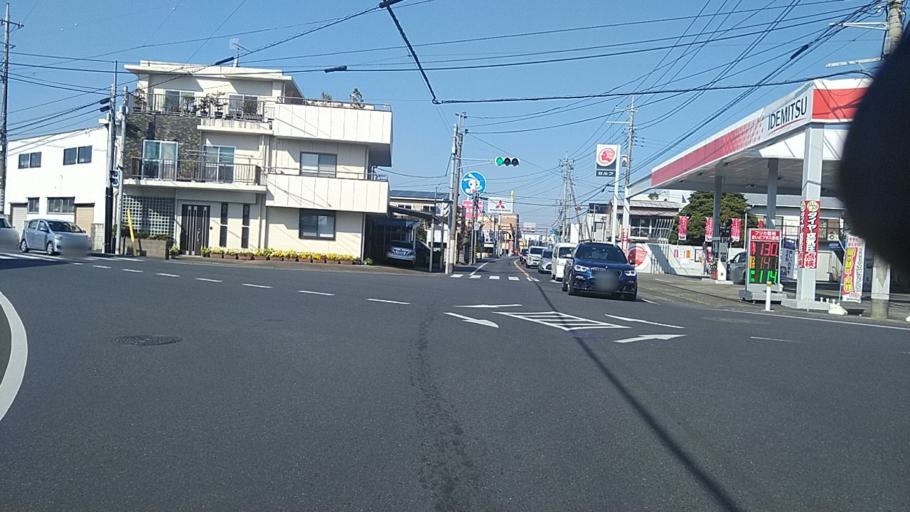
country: JP
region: Chiba
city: Mobara
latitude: 35.4326
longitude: 140.2935
